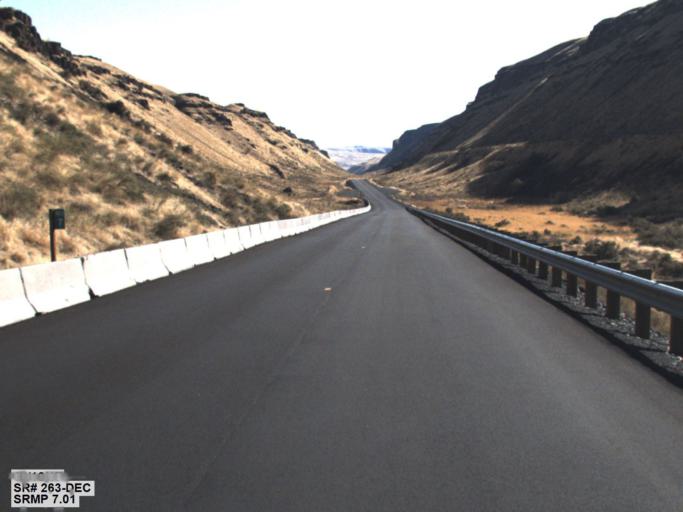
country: US
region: Washington
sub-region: Franklin County
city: Connell
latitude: 46.6154
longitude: -118.5562
